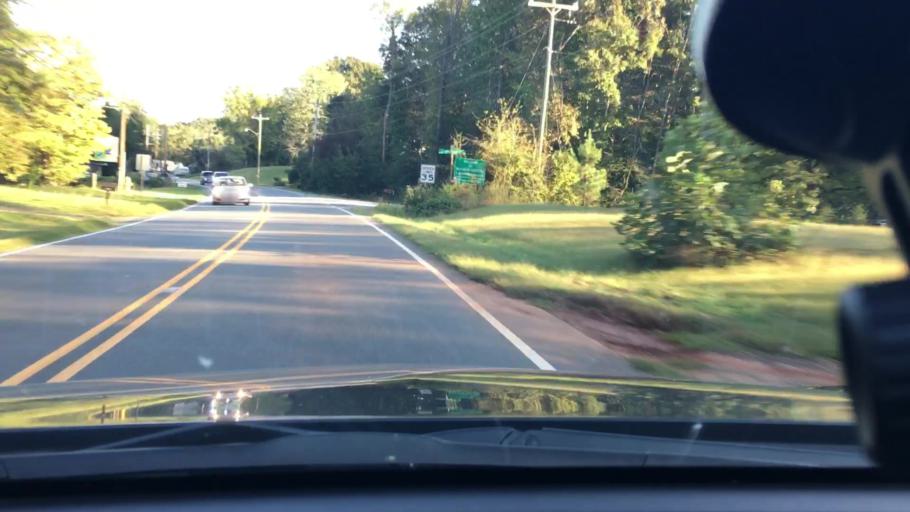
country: US
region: North Carolina
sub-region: Rutherford County
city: Rutherfordton
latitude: 35.3842
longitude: -81.9677
